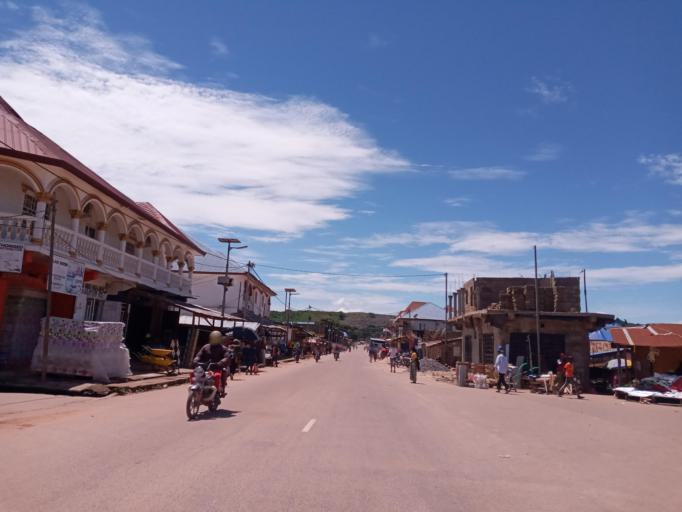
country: SL
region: Eastern Province
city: Koidu
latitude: 8.6435
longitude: -10.9707
